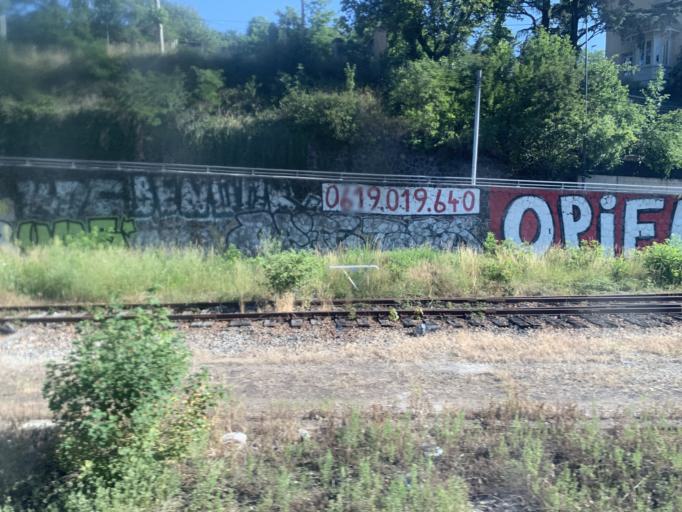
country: FR
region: Rhone-Alpes
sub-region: Departement de la Loire
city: Saint-Jean-Bonnefonds
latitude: 45.4349
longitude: 4.4434
